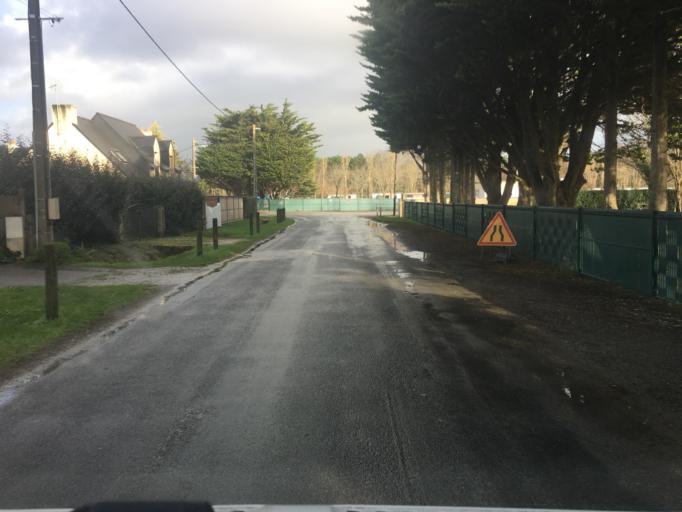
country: FR
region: Brittany
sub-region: Departement du Morbihan
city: Sarzeau
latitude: 47.4987
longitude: -2.7671
